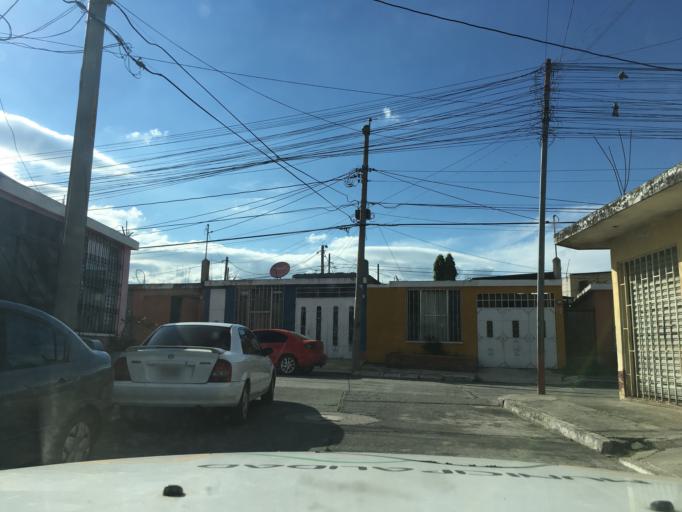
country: GT
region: Guatemala
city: Petapa
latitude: 14.4990
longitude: -90.5671
